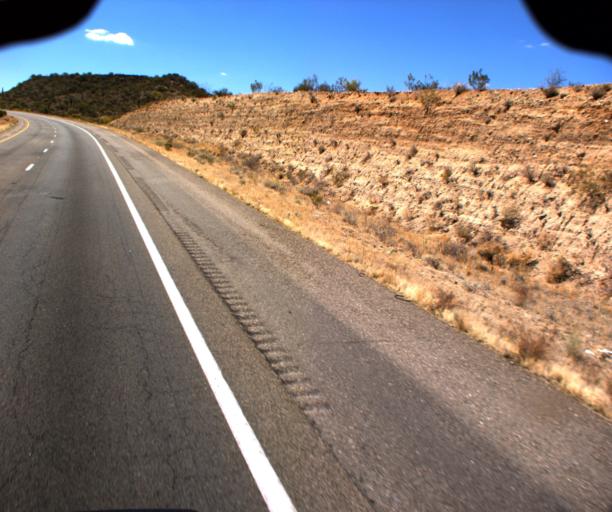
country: US
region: Arizona
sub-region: Yavapai County
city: Bagdad
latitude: 34.4382
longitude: -113.2604
